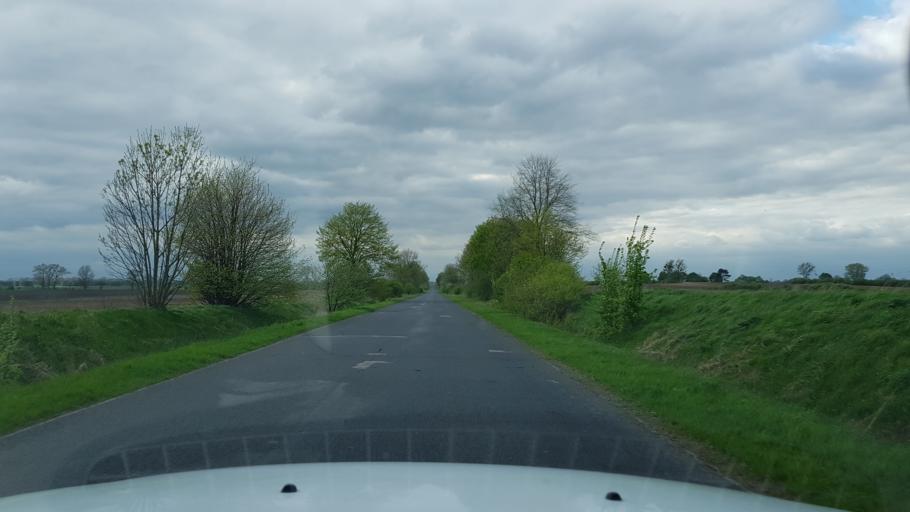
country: PL
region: West Pomeranian Voivodeship
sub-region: Powiat pyrzycki
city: Przelewice
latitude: 53.1382
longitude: 15.0321
